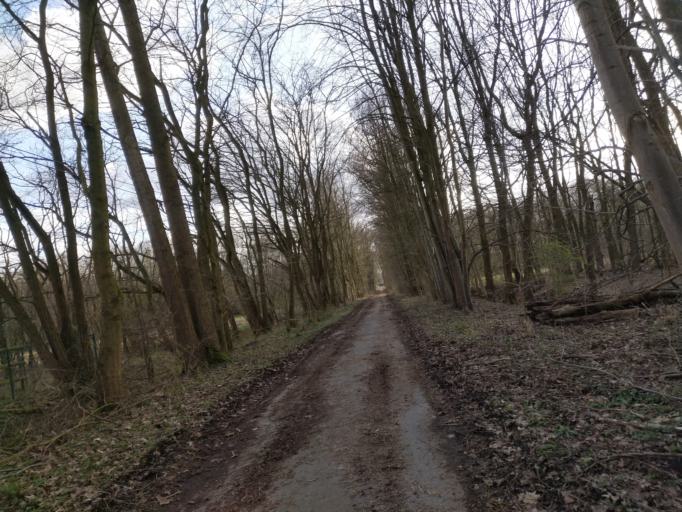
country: DE
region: North Rhine-Westphalia
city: Olfen
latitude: 51.6944
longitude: 7.3236
